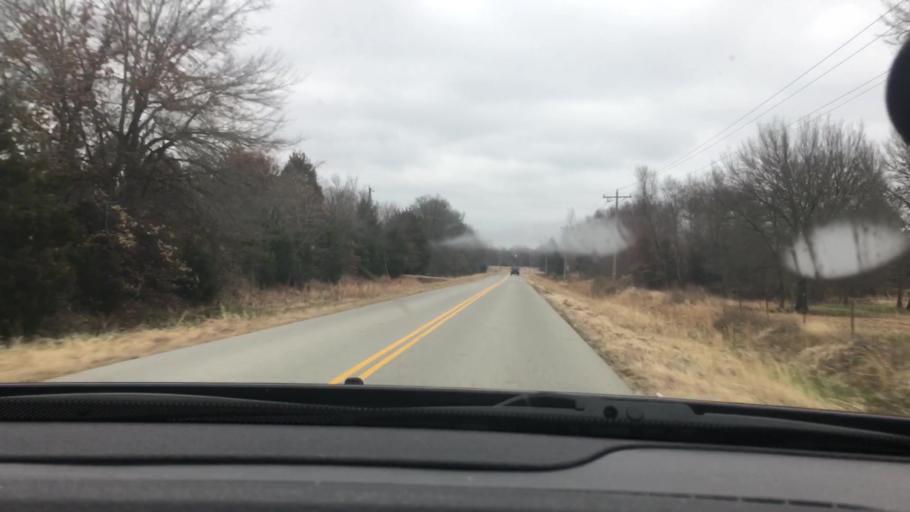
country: US
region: Oklahoma
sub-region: Atoka County
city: Atoka
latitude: 34.3411
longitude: -96.0754
